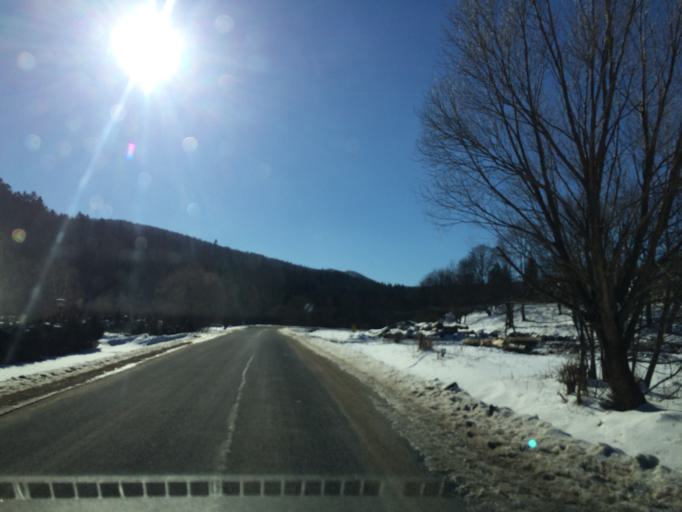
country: PL
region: Subcarpathian Voivodeship
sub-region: Powiat bieszczadzki
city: Lutowiska
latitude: 49.1648
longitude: 22.6915
